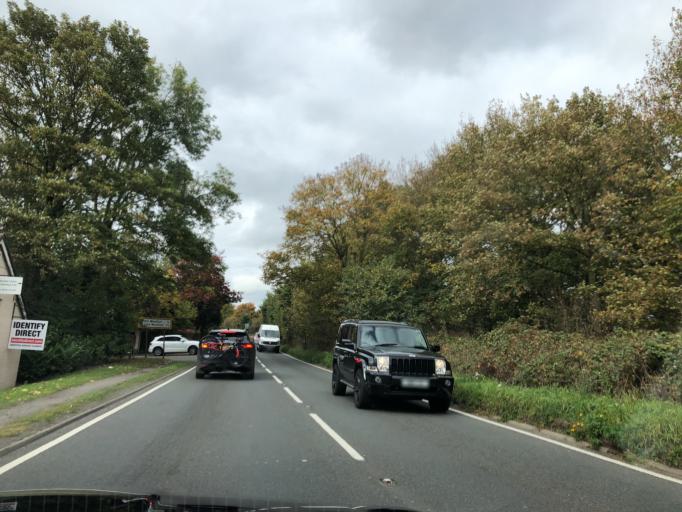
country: GB
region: England
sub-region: Warwickshire
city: Royal Leamington Spa
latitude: 52.3194
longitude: -1.5443
